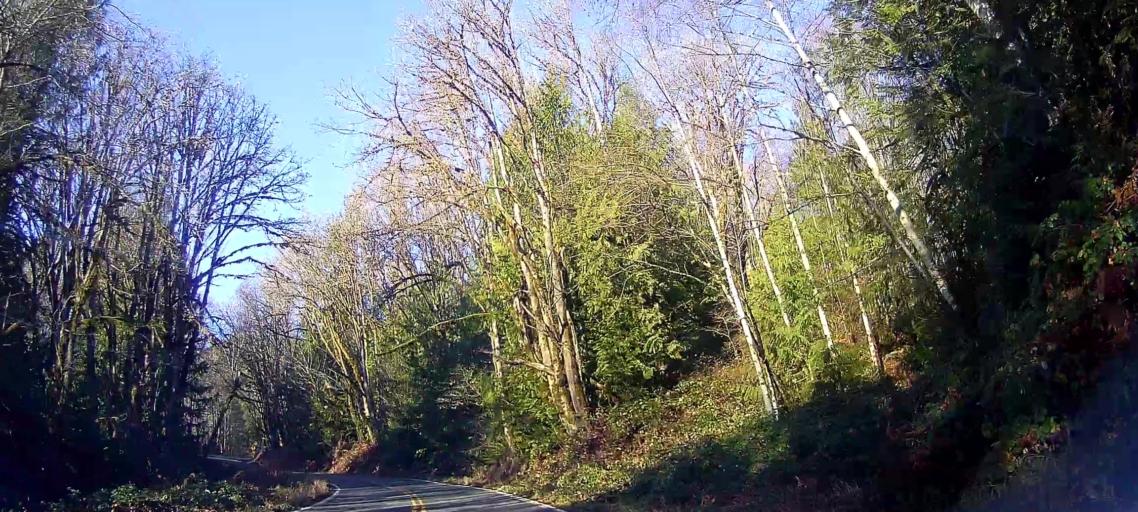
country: US
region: Washington
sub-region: Snohomish County
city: Darrington
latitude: 48.5408
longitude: -121.7638
